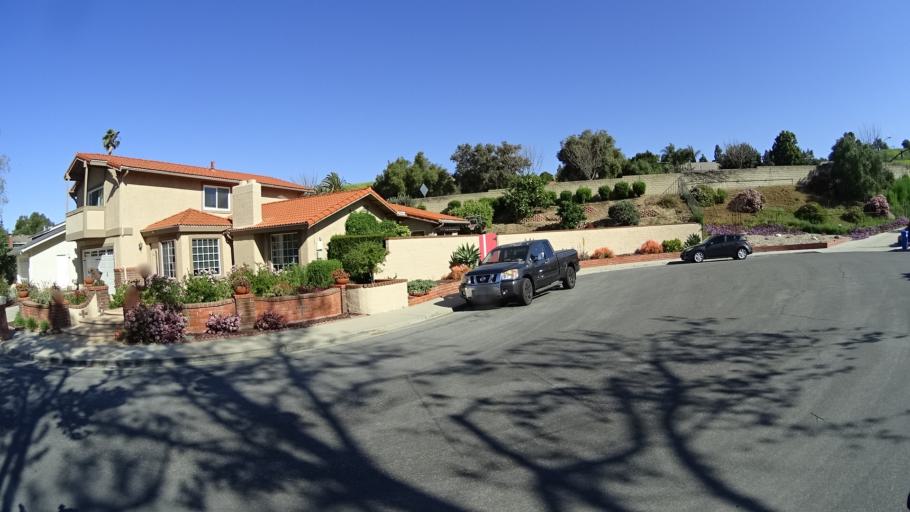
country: US
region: California
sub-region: Ventura County
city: Thousand Oaks
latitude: 34.2117
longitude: -118.8323
